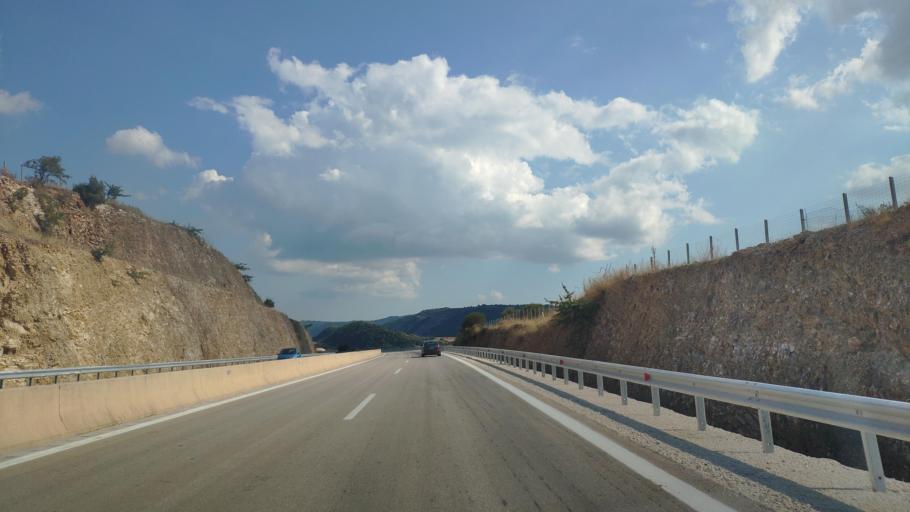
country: GR
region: West Greece
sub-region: Nomos Aitolias kai Akarnanias
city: Katouna
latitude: 38.8061
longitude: 21.1308
